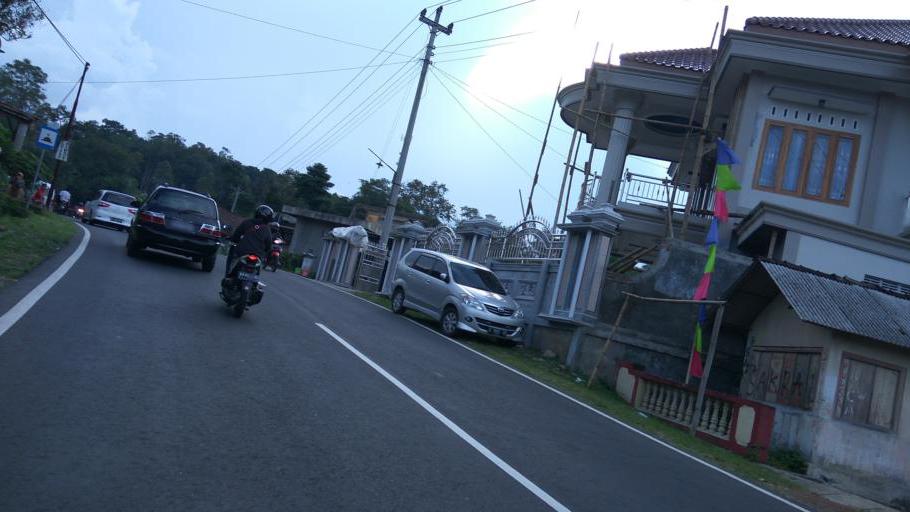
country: ID
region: Central Java
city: Gunung Kendil
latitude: -7.3727
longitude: 110.4463
